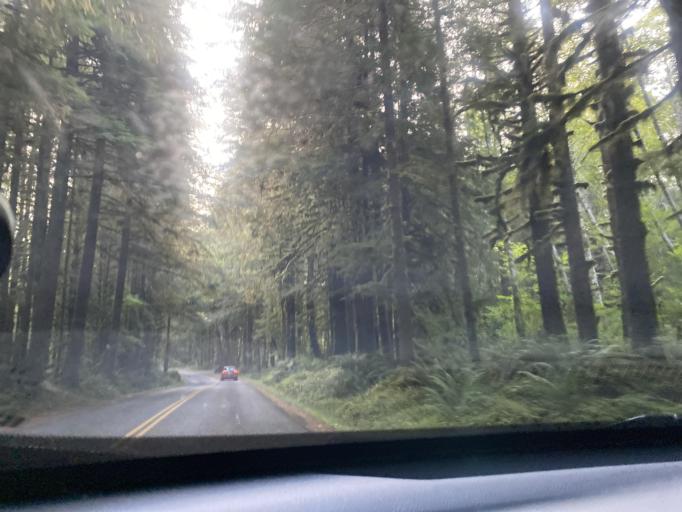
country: US
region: Washington
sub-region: Clallam County
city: Forks
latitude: 47.8168
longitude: -124.0449
